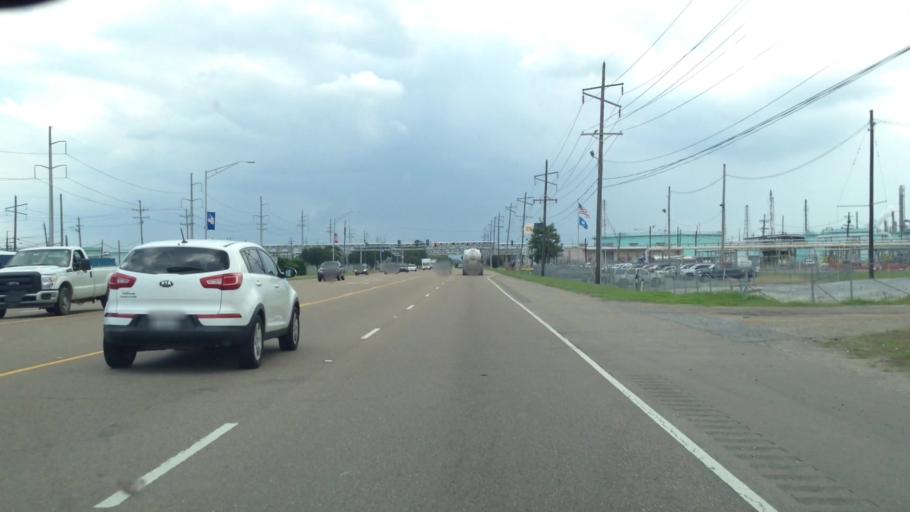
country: US
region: Louisiana
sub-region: Saint Charles Parish
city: Norco
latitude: 30.0140
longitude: -90.4051
